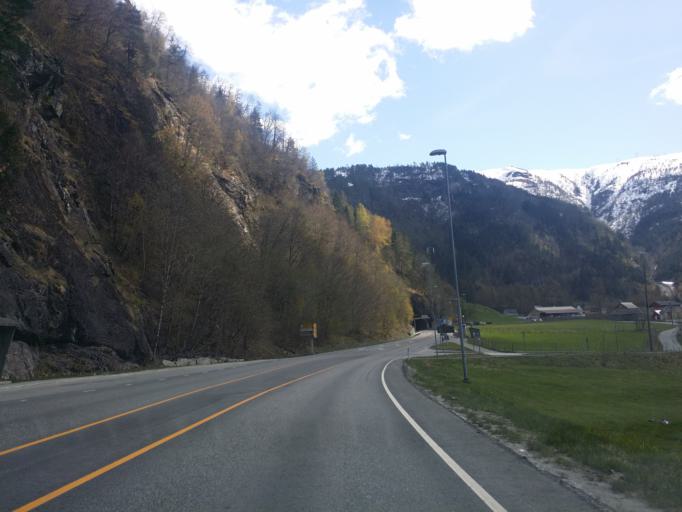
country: NO
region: Hordaland
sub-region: Granvin
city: Granvin
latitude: 60.5354
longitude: 6.7336
